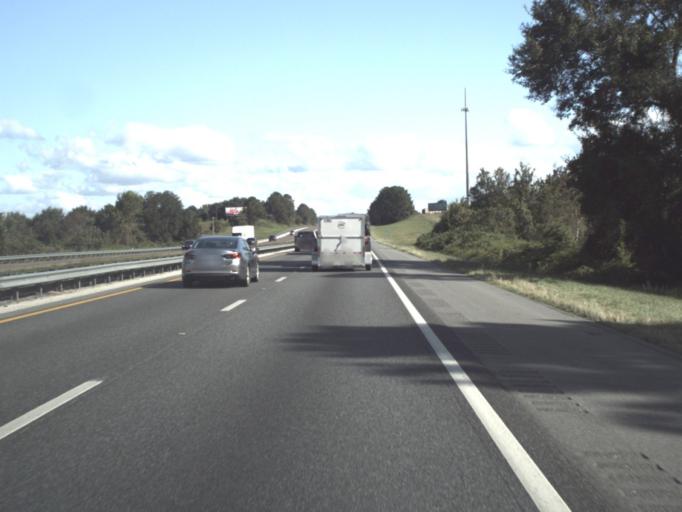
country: US
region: Florida
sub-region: Lake County
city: Minneola
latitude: 28.6405
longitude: -81.7865
